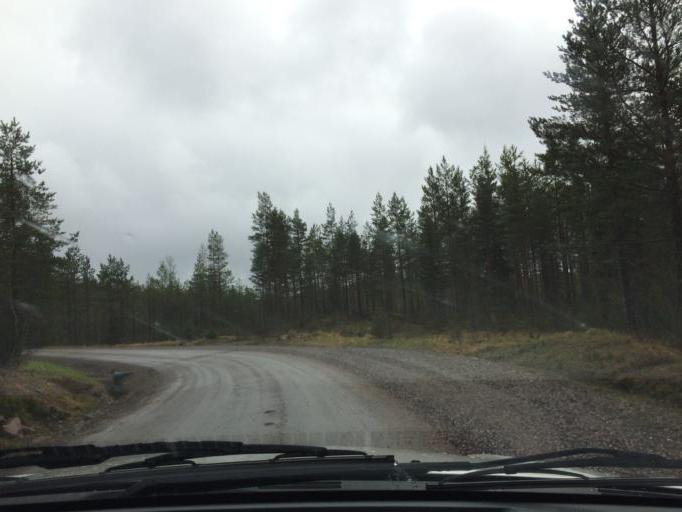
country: SE
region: OErebro
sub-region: Hallefors Kommun
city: Haellefors
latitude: 60.0207
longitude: 14.5662
